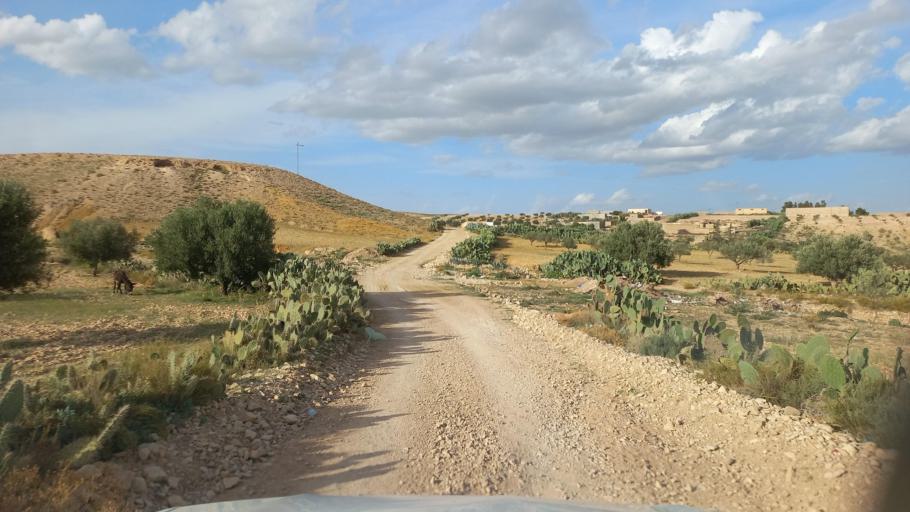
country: TN
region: Al Qasrayn
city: Sbiba
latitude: 35.4511
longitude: 9.0830
